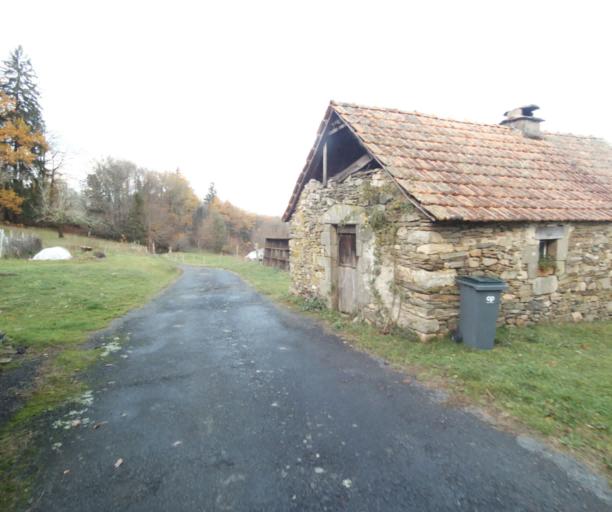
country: FR
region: Limousin
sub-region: Departement de la Correze
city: Cornil
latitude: 45.1985
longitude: 1.6932
